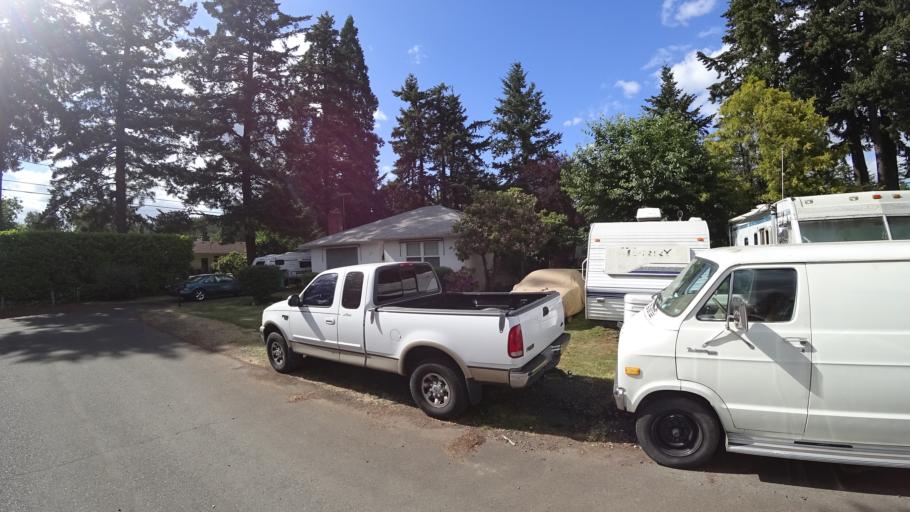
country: US
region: Oregon
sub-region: Multnomah County
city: Lents
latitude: 45.4953
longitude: -122.5426
